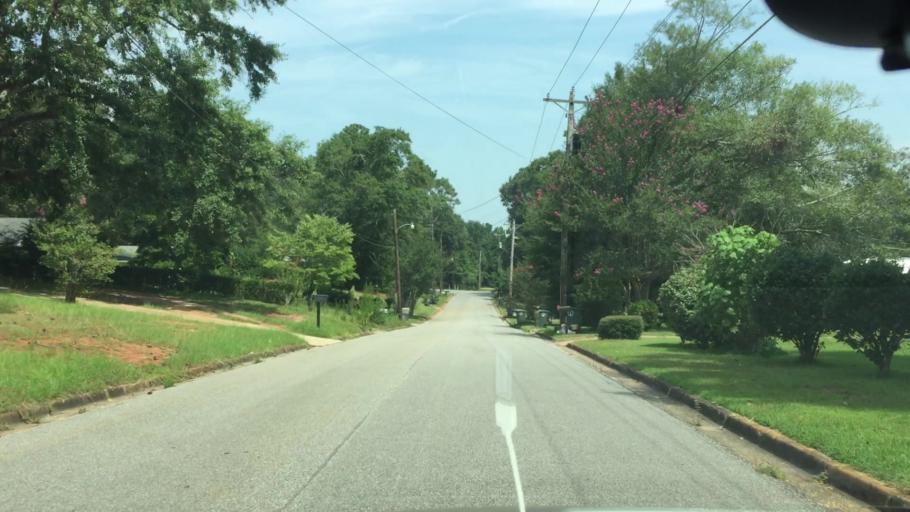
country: US
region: Alabama
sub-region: Coffee County
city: Enterprise
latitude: 31.3327
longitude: -85.8122
